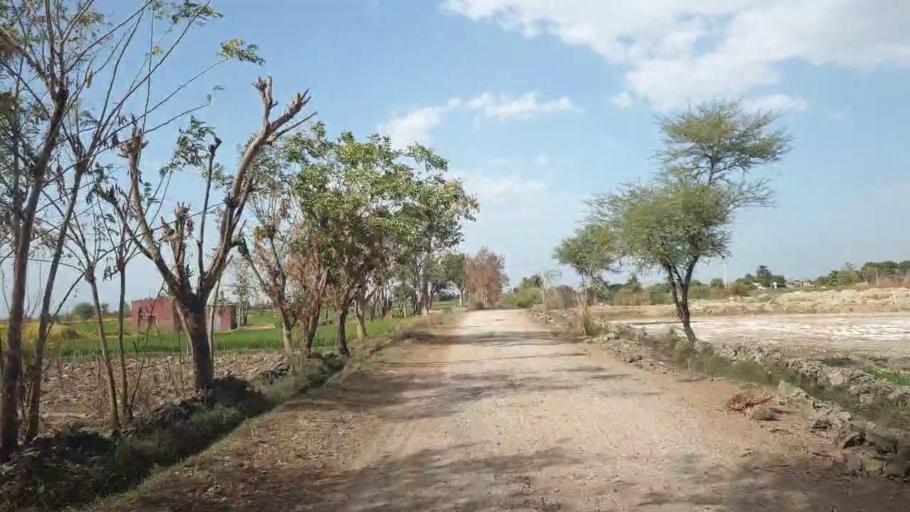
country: PK
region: Sindh
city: Shahdadpur
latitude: 26.0055
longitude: 68.4583
